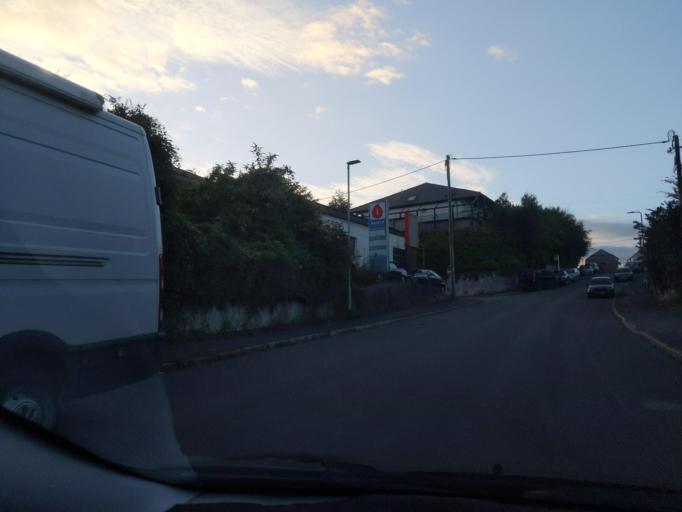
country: GB
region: England
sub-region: Plymouth
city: Plymstock
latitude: 50.3580
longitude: -4.0638
